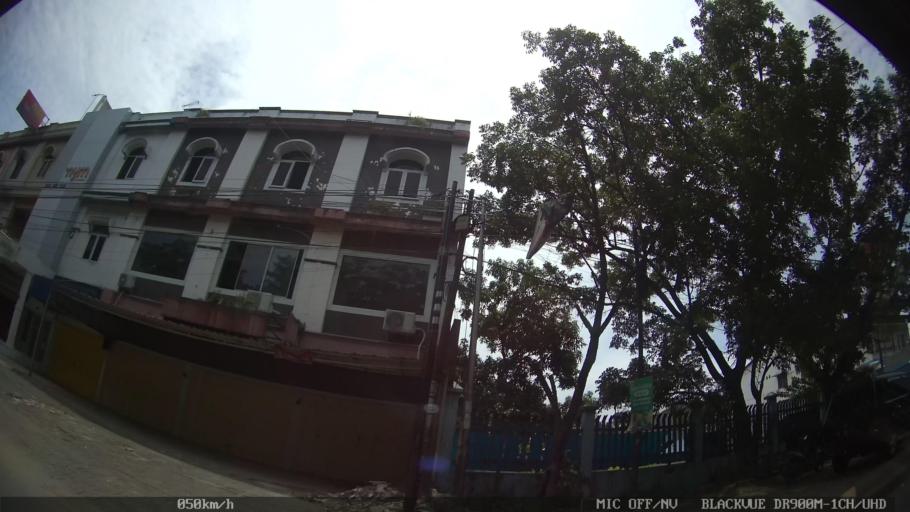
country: ID
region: North Sumatra
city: Sunggal
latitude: 3.5576
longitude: 98.6271
